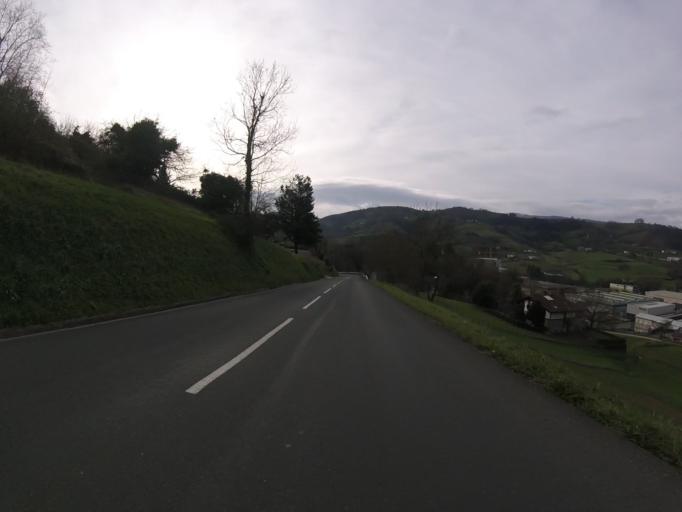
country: ES
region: Basque Country
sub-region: Provincia de Guipuzcoa
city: Azpeitia
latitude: 43.1747
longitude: -2.2490
